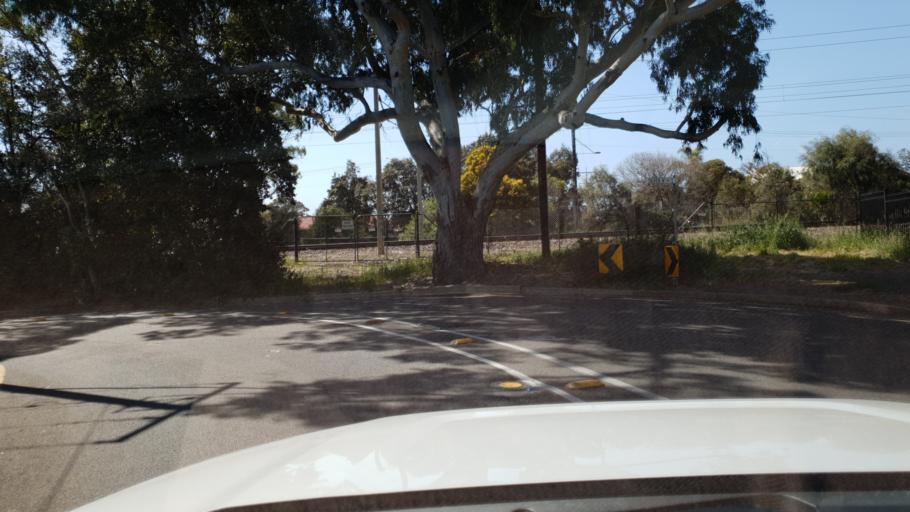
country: AU
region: South Australia
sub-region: Adelaide Hills
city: Seacliff
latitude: -35.0270
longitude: 138.5212
